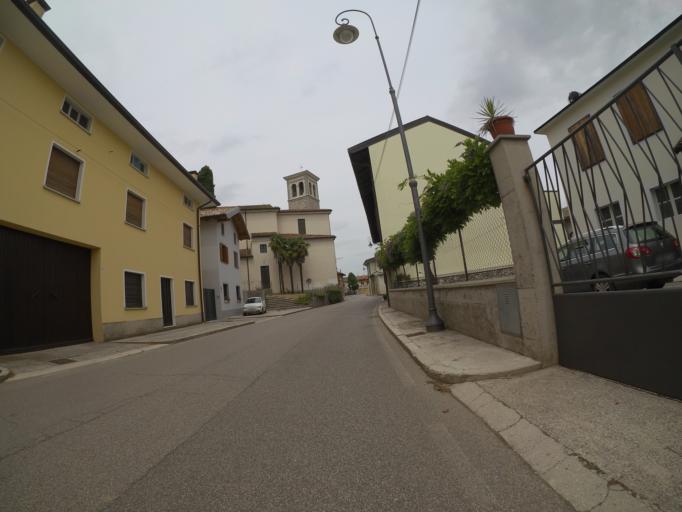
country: IT
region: Friuli Venezia Giulia
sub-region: Provincia di Udine
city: Basiliano-Vissandone
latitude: 46.0385
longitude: 13.1024
